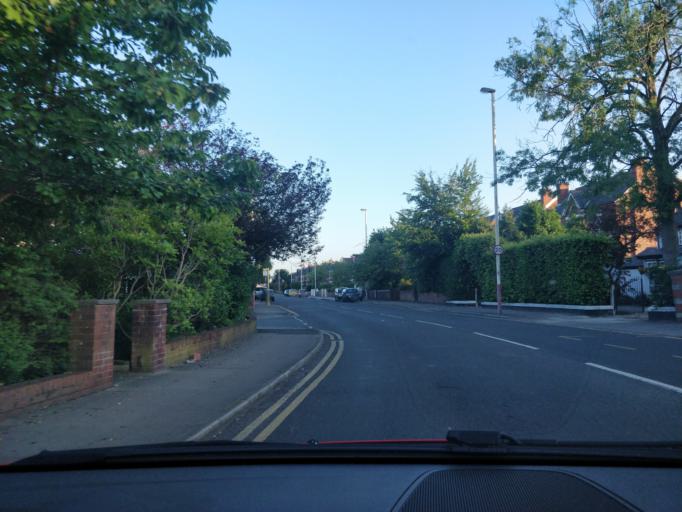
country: GB
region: England
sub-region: Sefton
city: Southport
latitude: 53.6571
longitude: -2.9659
